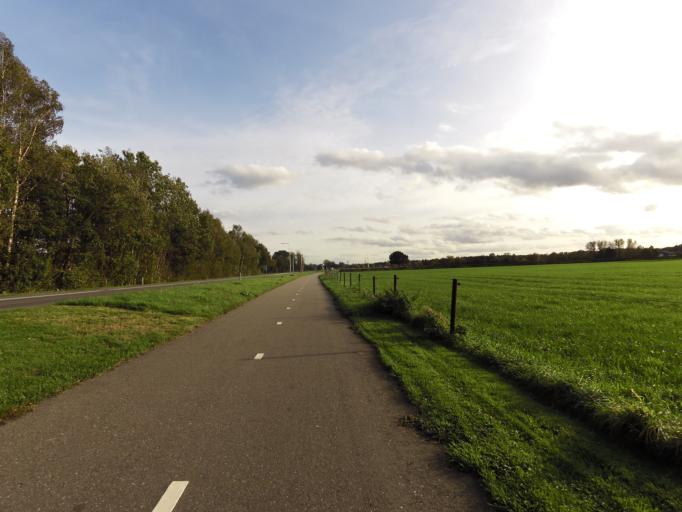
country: NL
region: Gelderland
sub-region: Gemeente Bronckhorst
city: Baak
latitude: 52.0145
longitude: 6.2268
